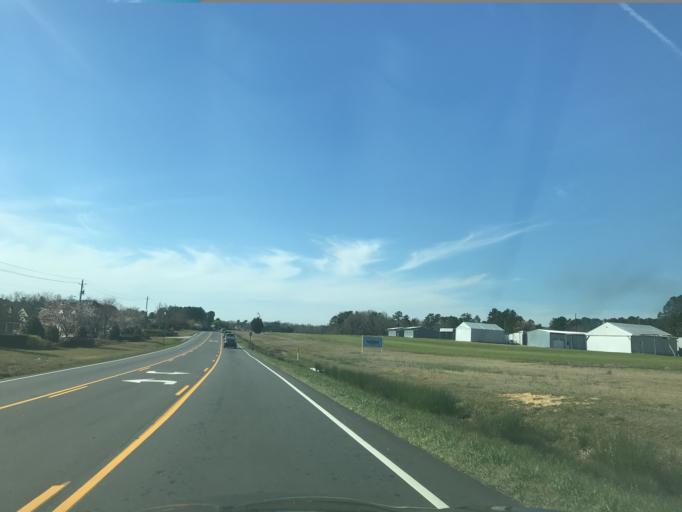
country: US
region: North Carolina
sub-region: Harnett County
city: Angier
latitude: 35.5409
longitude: -78.7482
